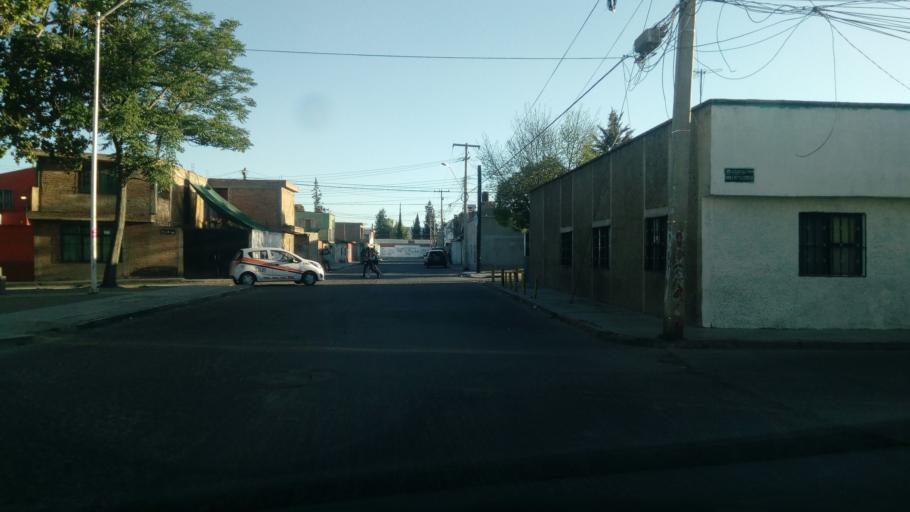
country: MX
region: Durango
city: Victoria de Durango
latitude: 23.9987
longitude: -104.6803
